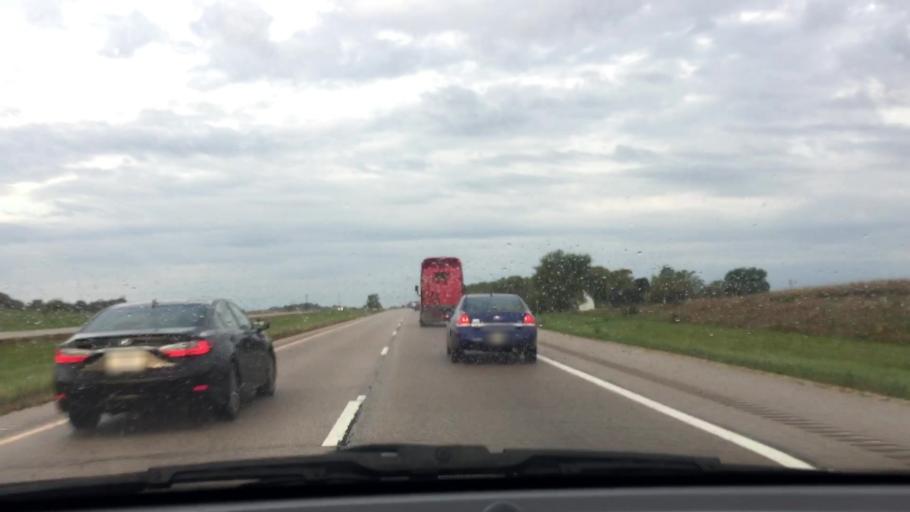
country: US
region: Wisconsin
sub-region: Rock County
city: Clinton
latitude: 42.5724
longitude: -88.8301
